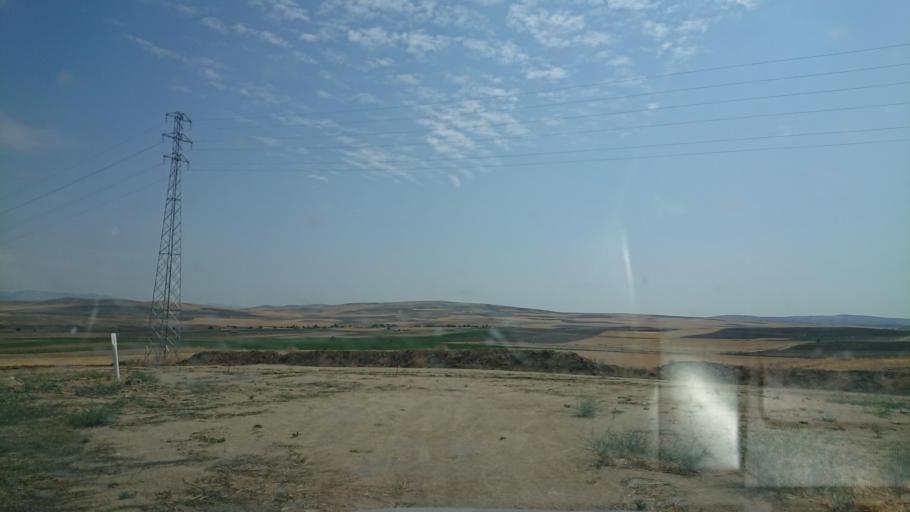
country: TR
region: Aksaray
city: Sariyahsi
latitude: 38.9550
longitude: 33.9124
